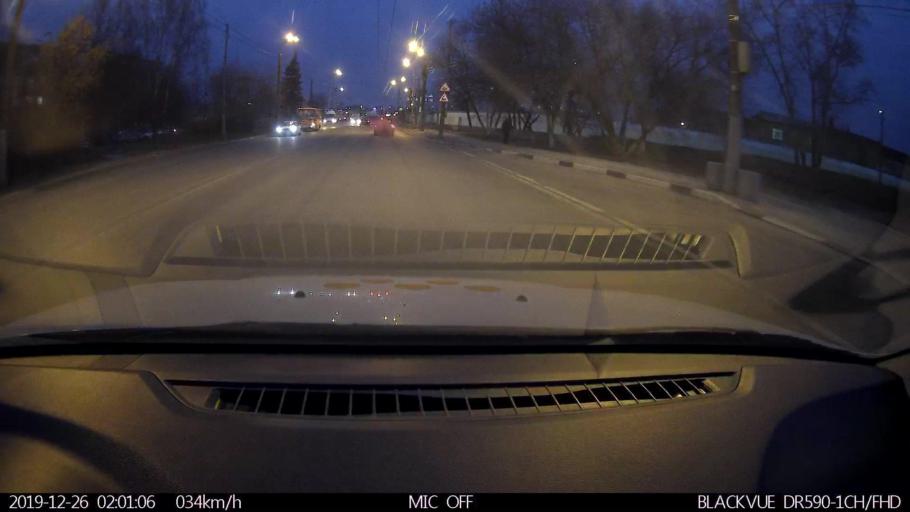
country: RU
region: Nizjnij Novgorod
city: Nizhniy Novgorod
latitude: 56.3111
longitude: 43.9454
